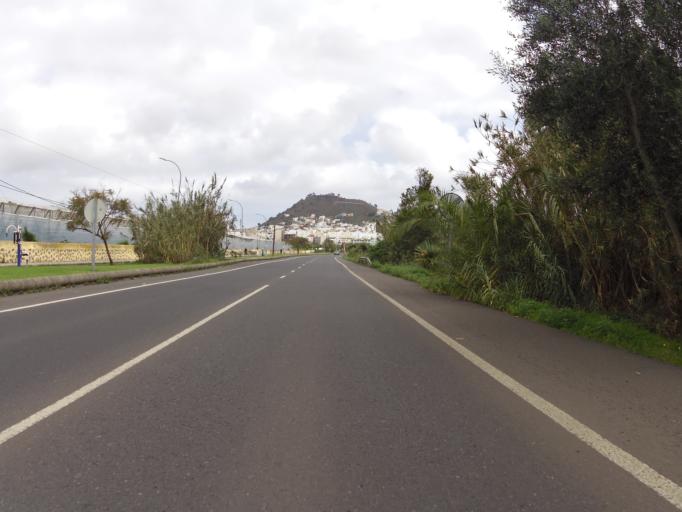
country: ES
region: Canary Islands
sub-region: Provincia de Las Palmas
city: Arucas
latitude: 28.1110
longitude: -15.5259
